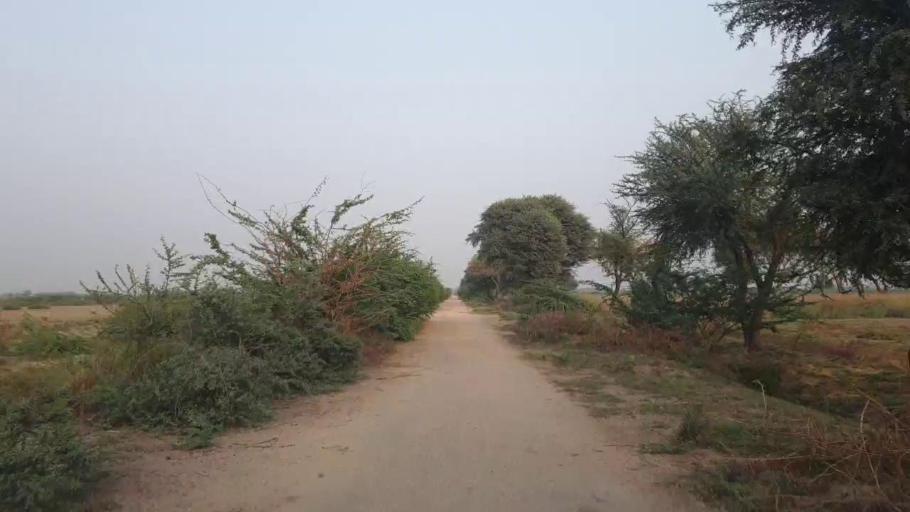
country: PK
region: Sindh
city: Mirpur Batoro
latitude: 24.6516
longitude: 68.3733
